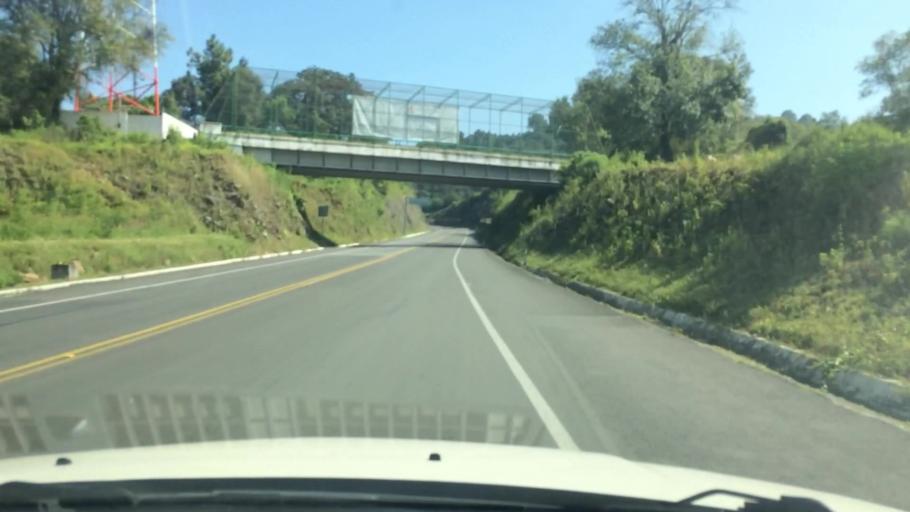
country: MX
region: Mexico
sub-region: Valle de Bravo
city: Colonia Rincon Villa del Valle
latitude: 19.2042
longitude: -100.0995
